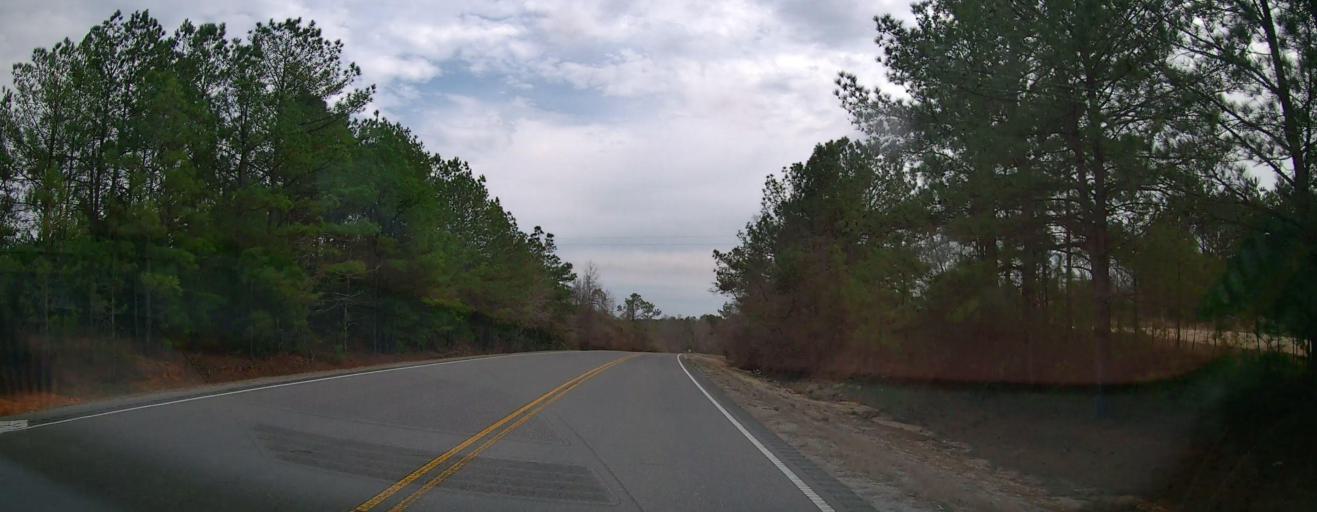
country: US
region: Alabama
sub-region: Marion County
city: Guin
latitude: 34.0285
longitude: -87.9419
